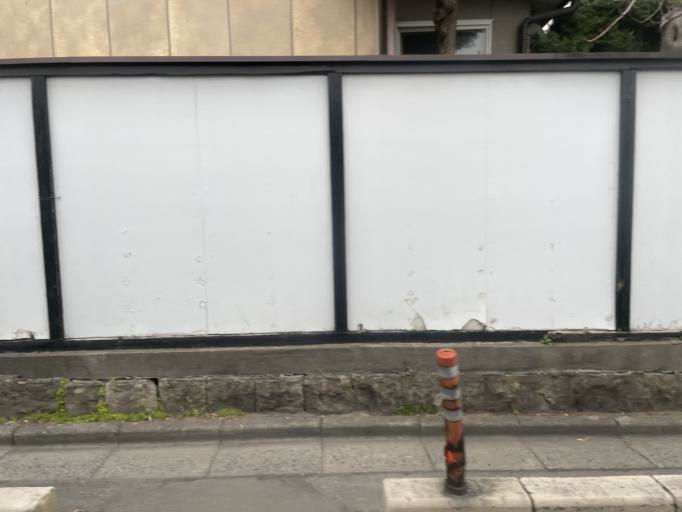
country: JP
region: Aomori
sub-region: Hachinohe Shi
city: Uchimaru
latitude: 40.5054
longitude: 141.4828
